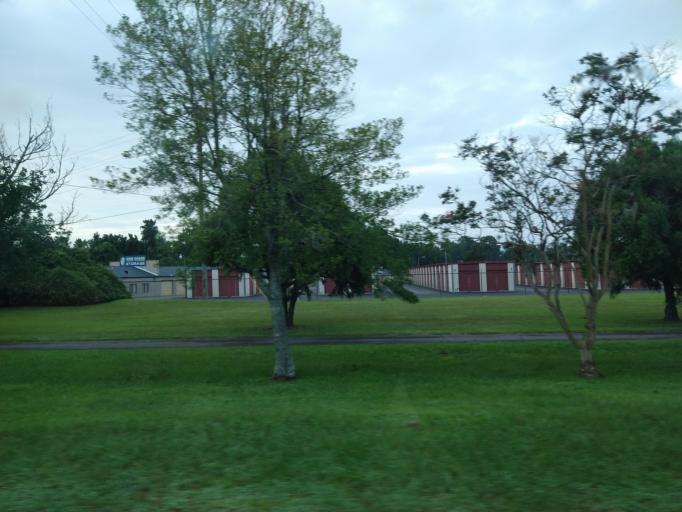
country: US
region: North Carolina
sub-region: Onslow County
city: Jacksonville
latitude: 34.7583
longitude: -77.4189
